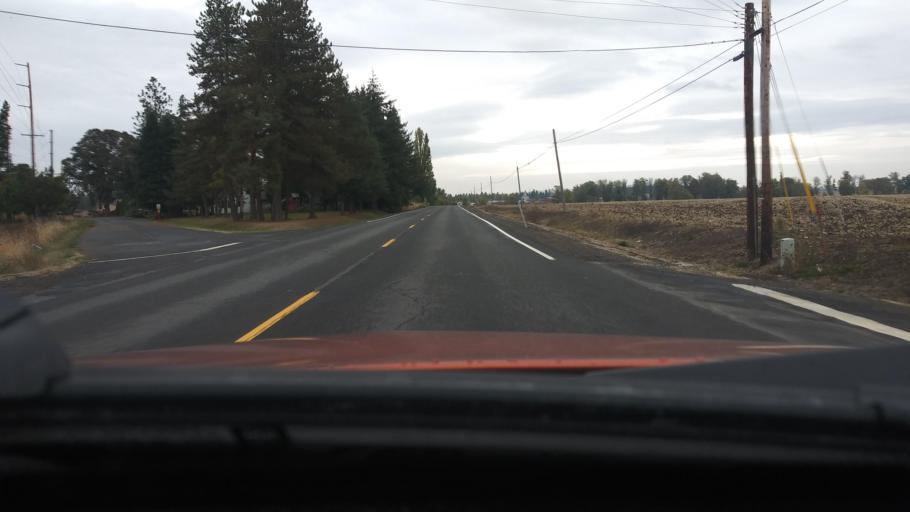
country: US
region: Oregon
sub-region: Washington County
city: Banks
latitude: 45.5794
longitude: -123.1122
